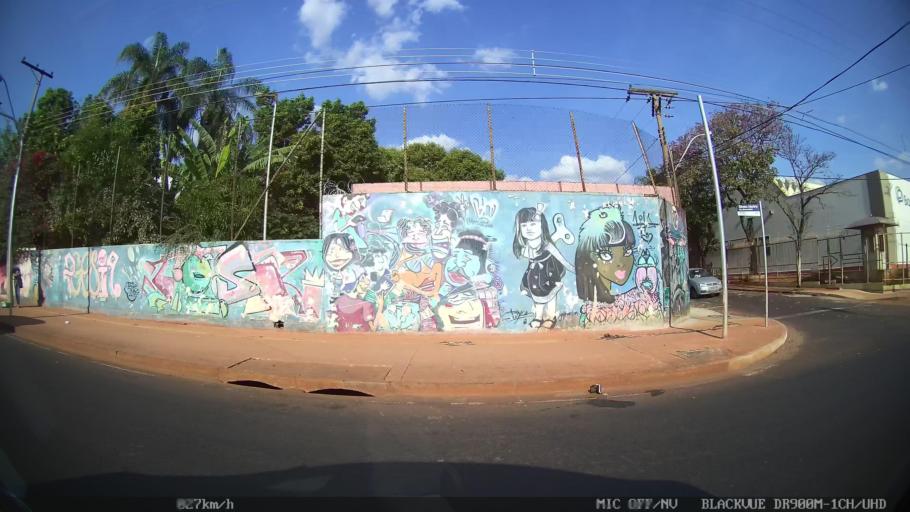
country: BR
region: Sao Paulo
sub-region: Ribeirao Preto
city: Ribeirao Preto
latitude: -21.1654
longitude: -47.8131
